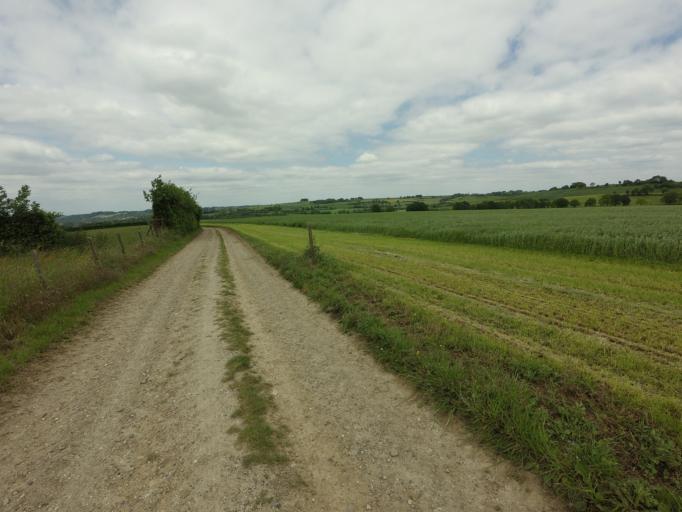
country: NL
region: Limburg
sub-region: Valkenburg aan de Geul
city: Schin op Geul
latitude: 50.8346
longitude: 5.9045
